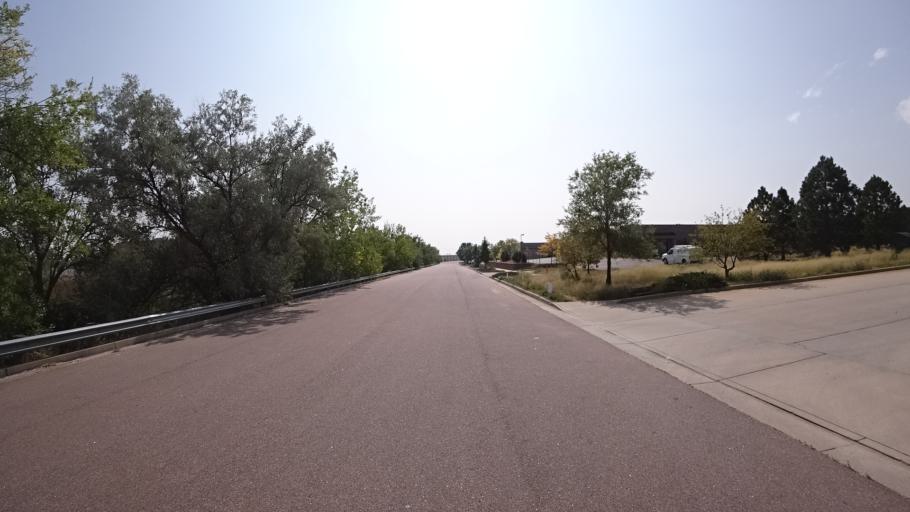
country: US
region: Colorado
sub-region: El Paso County
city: Cimarron Hills
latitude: 38.8383
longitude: -104.7413
